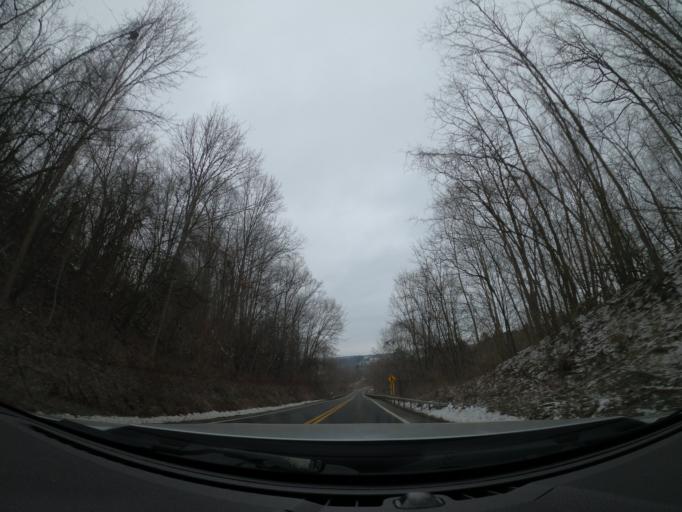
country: US
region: New York
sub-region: Cayuga County
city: Moravia
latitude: 42.6526
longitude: -76.4397
